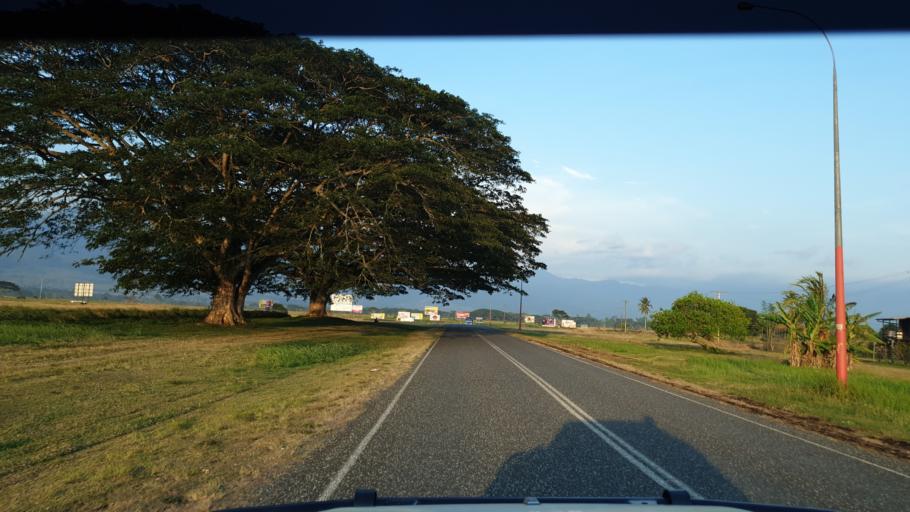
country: PG
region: Morobe
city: Lae
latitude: -6.5653
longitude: 146.7446
